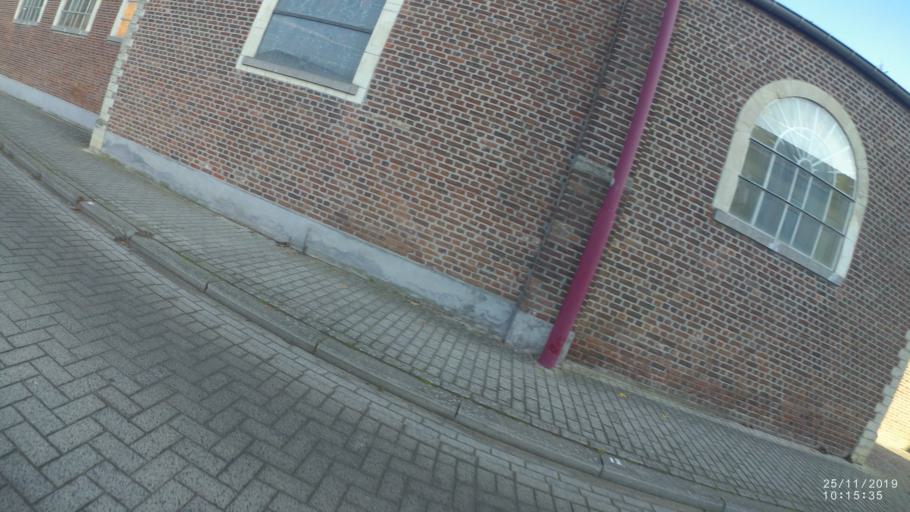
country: BE
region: Flanders
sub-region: Provincie Vlaams-Brabant
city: Diest
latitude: 51.0035
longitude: 5.0148
